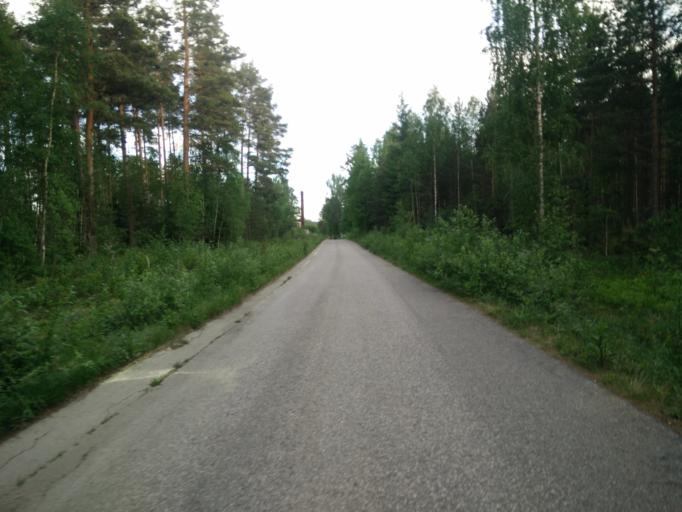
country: SE
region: Vaermland
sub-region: Hagfors Kommun
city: Hagfors
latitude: 60.0118
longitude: 13.5939
